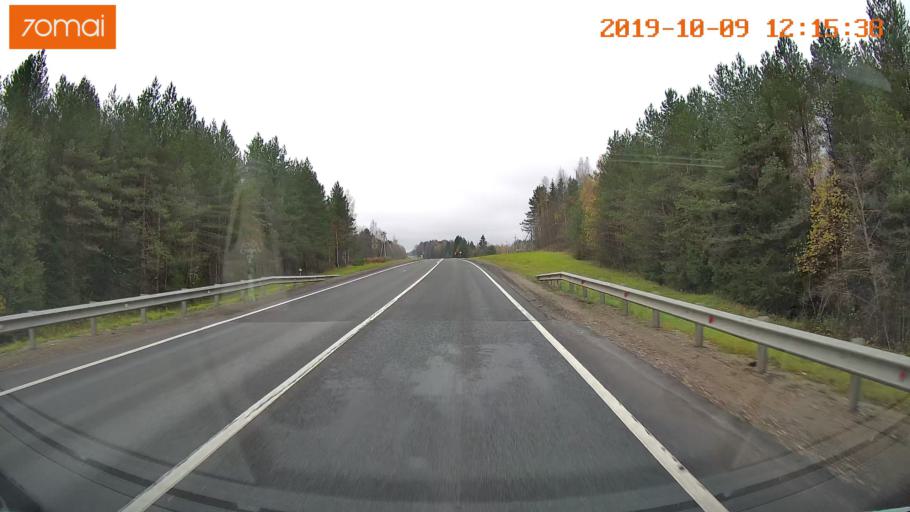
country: RU
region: Jaroslavl
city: Prechistoye
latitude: 58.4806
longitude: 40.3231
